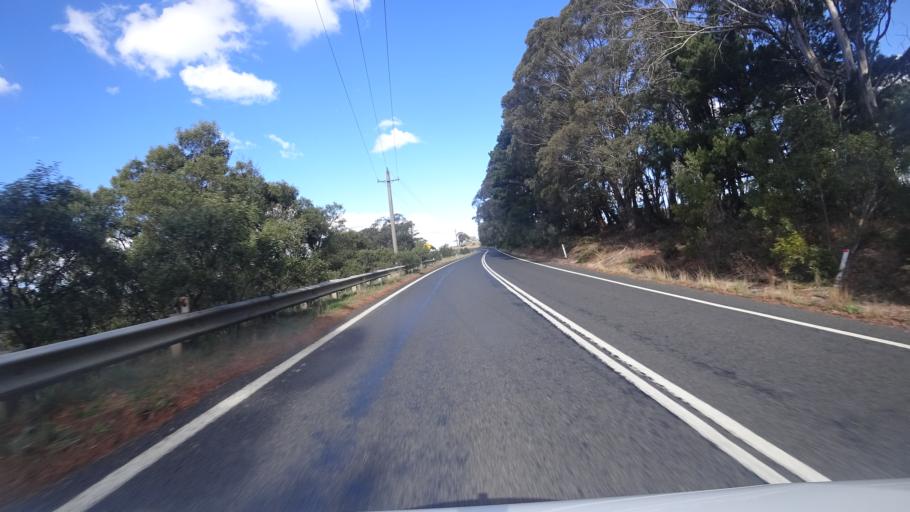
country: AU
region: New South Wales
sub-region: Lithgow
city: Bowenfels
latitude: -33.6366
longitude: 150.0677
